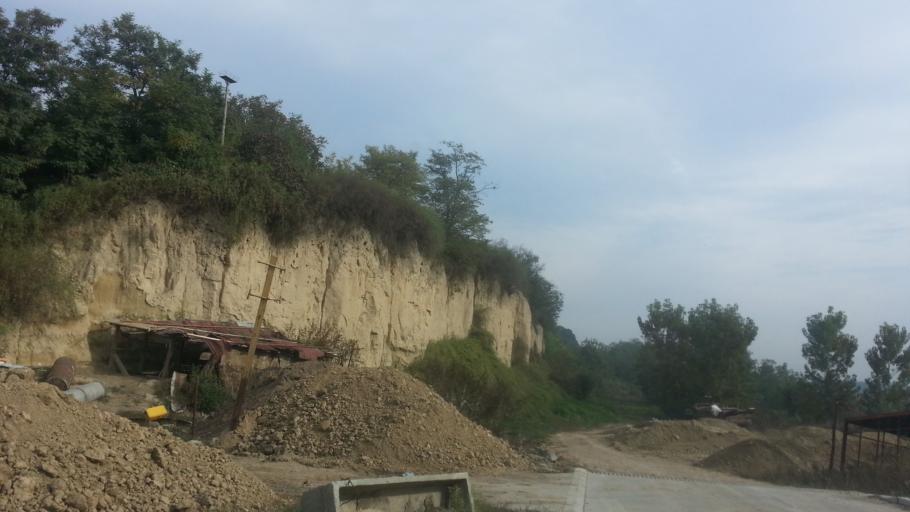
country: RS
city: Stari Banovci
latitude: 45.0005
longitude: 20.3045
